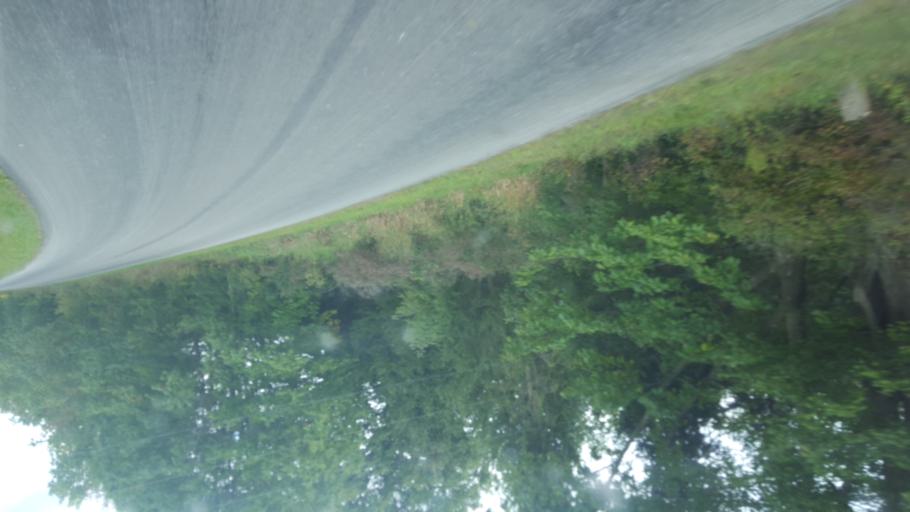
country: US
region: Pennsylvania
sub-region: Crawford County
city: Conneaut Lakeshore
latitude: 41.5035
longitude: -80.2749
